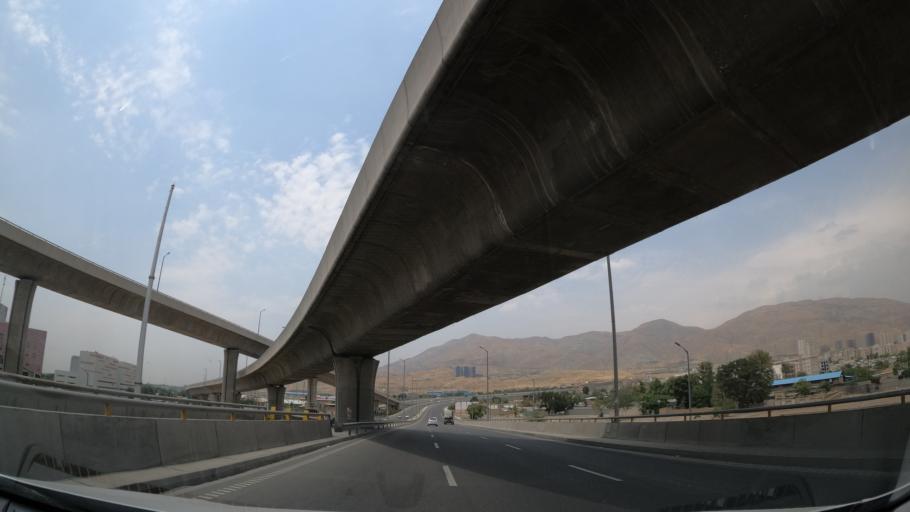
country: IR
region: Tehran
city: Shahr-e Qods
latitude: 35.7335
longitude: 51.1237
